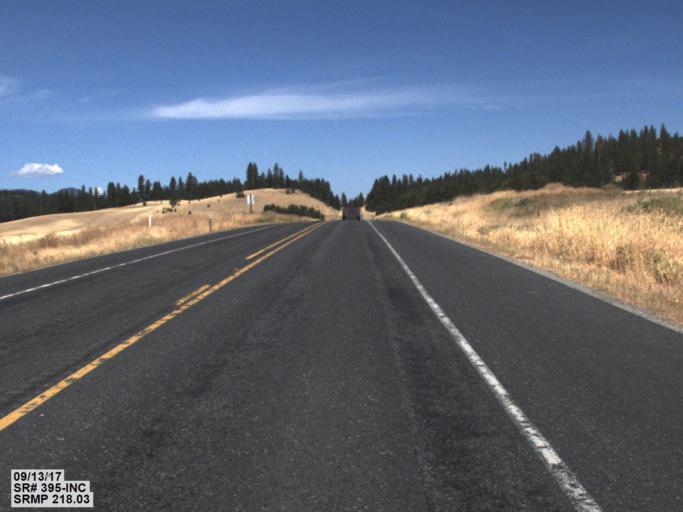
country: US
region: Washington
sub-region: Stevens County
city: Chewelah
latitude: 48.3878
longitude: -117.8441
